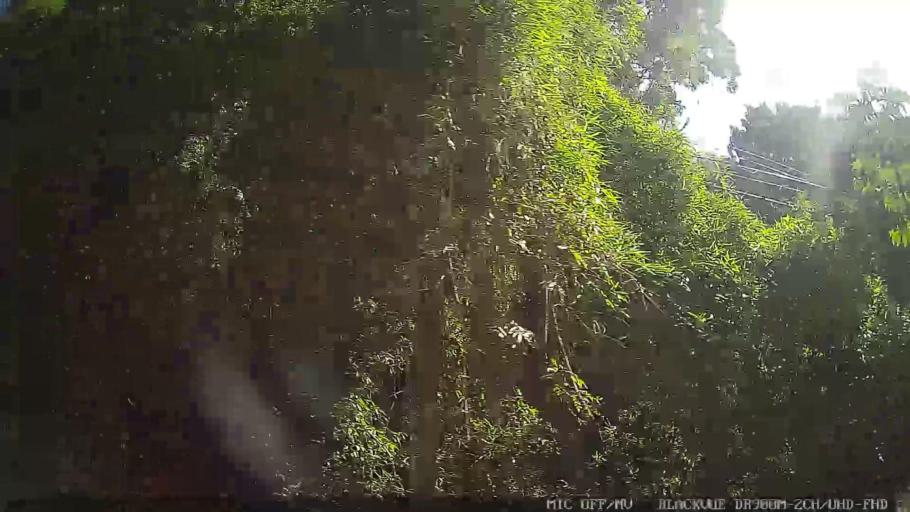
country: BR
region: Sao Paulo
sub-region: Santos
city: Santos
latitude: -23.9990
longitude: -46.3116
